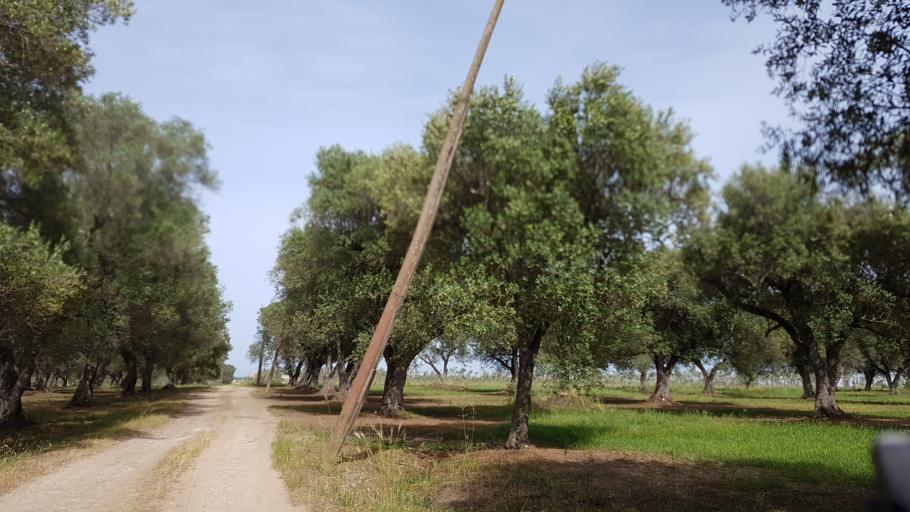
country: IT
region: Apulia
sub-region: Provincia di Brindisi
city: La Rosa
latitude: 40.5907
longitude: 18.0048
